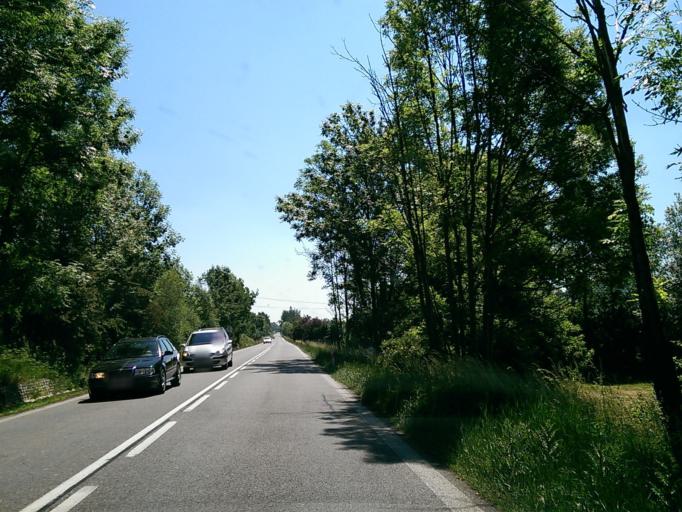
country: CZ
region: Liberecky
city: Rovensko pod Troskami
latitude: 50.5430
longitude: 15.2234
